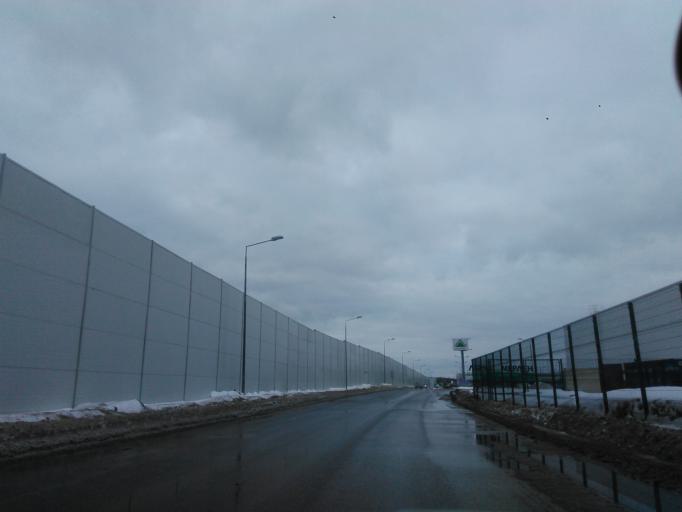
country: RU
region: Moskovskaya
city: Rzhavki
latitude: 55.9974
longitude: 37.2567
